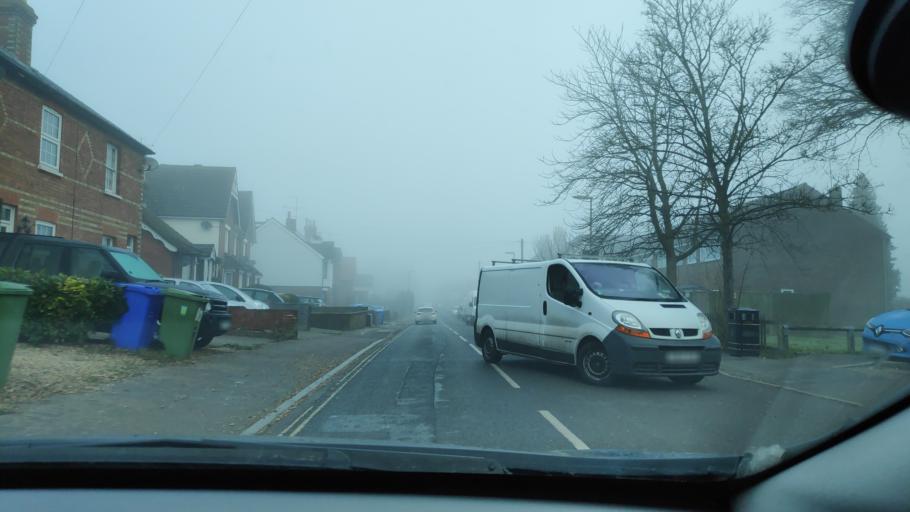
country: GB
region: England
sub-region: Hampshire
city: Farnborough
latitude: 51.2783
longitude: -0.7378
